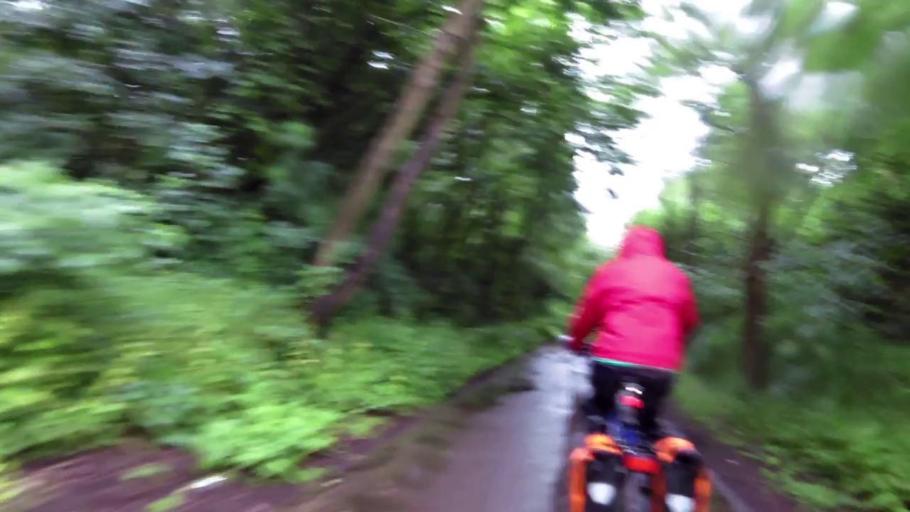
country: PL
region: West Pomeranian Voivodeship
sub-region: Powiat kolobrzeski
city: Ustronie Morskie
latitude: 54.2330
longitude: 15.8212
